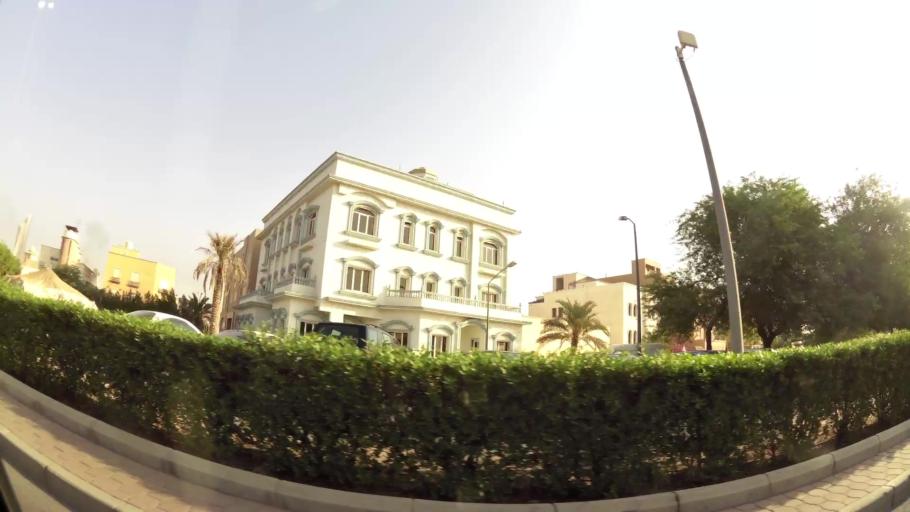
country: KW
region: Al Asimah
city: Ad Dasmah
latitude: 29.3582
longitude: 48.0017
